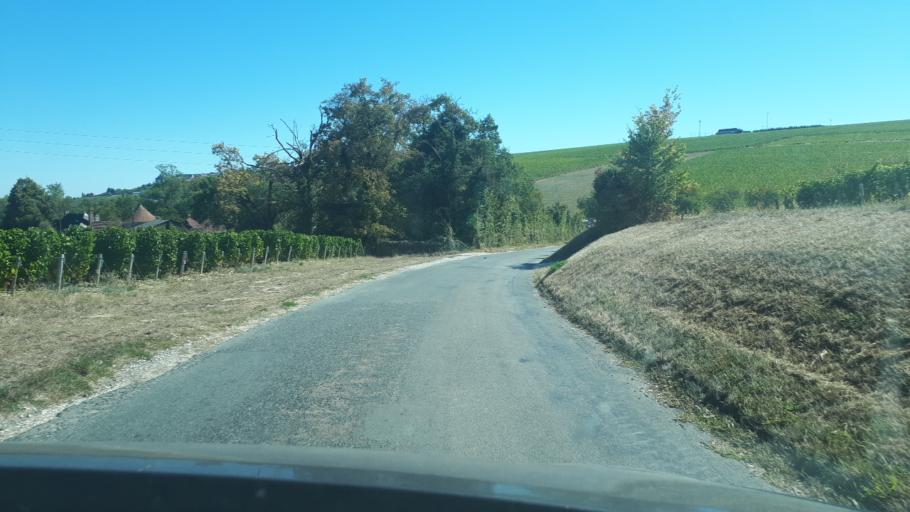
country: FR
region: Centre
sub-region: Departement du Cher
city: Sancerre
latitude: 47.3260
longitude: 2.8117
